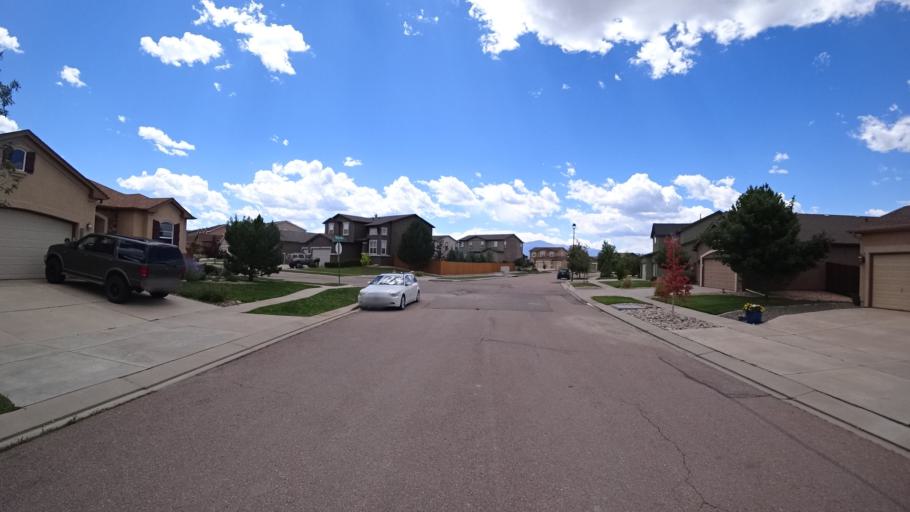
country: US
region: Colorado
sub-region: El Paso County
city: Black Forest
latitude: 38.9496
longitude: -104.7129
